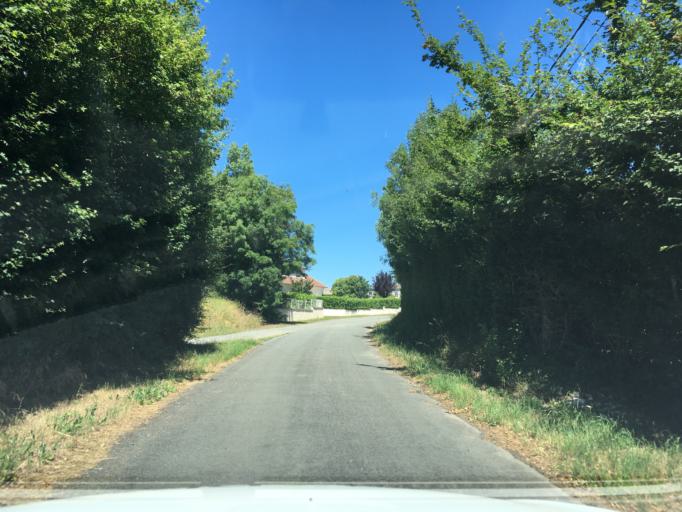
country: FR
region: Poitou-Charentes
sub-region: Departement des Deux-Sevres
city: Aiffres
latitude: 46.3150
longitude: -0.4236
